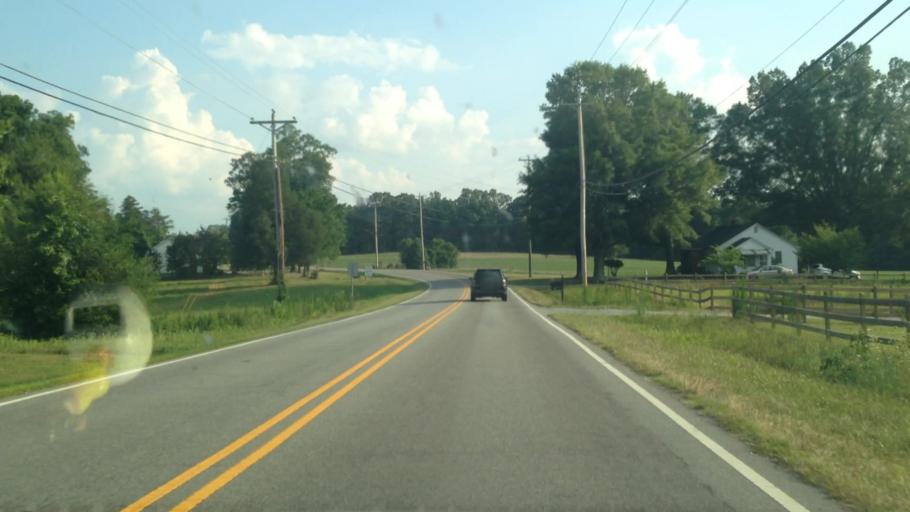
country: US
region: North Carolina
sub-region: Guilford County
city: High Point
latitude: 36.0032
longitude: -80.0623
